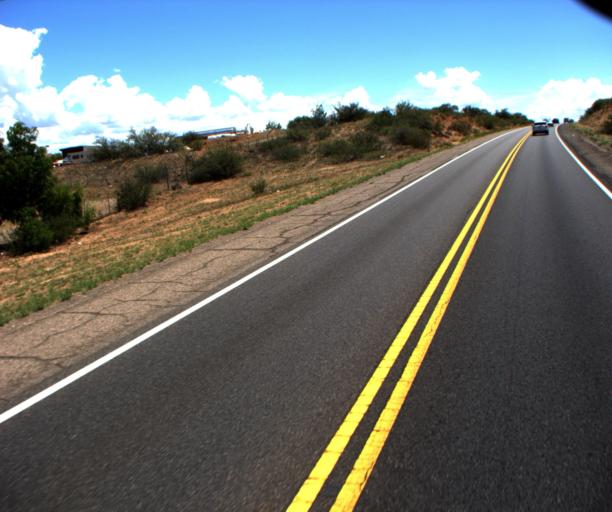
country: US
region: Arizona
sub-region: Yavapai County
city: Camp Verde
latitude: 34.6168
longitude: -111.9174
